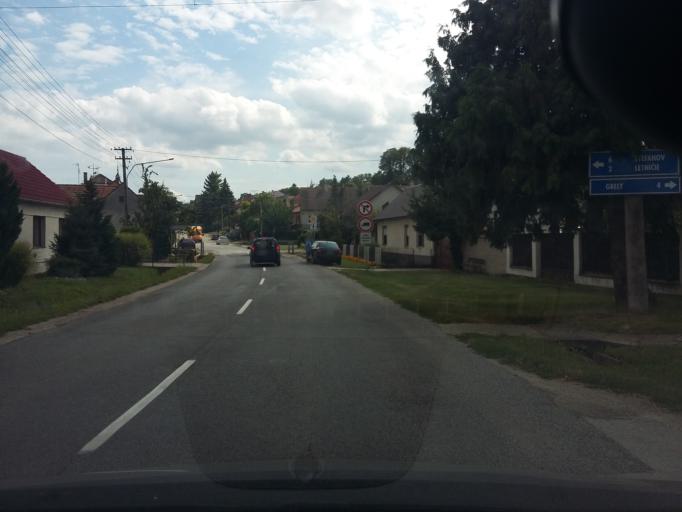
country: SK
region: Trnavsky
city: Gbely
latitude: 48.7247
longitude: 17.1611
